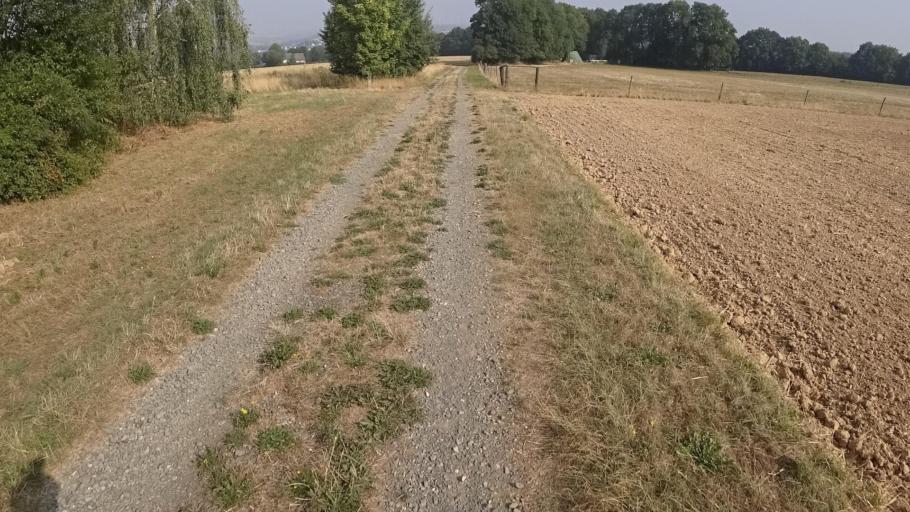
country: DE
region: Rheinland-Pfalz
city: Simmern
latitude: 49.9675
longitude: 7.5234
